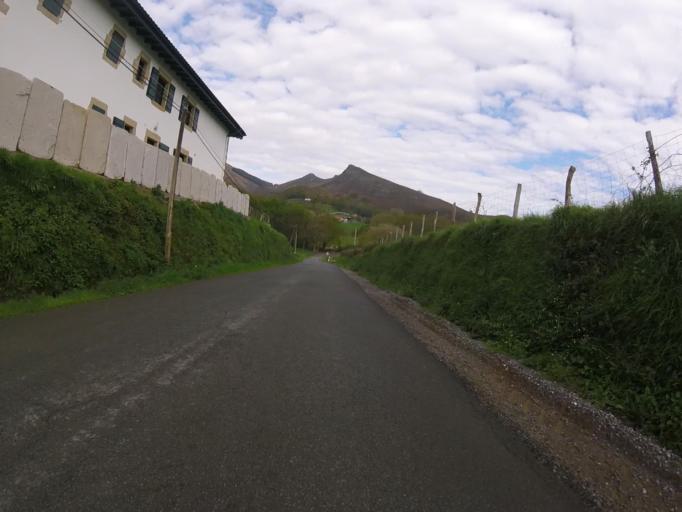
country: FR
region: Aquitaine
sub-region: Departement des Pyrenees-Atlantiques
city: Sare
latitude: 43.3018
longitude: -1.5914
